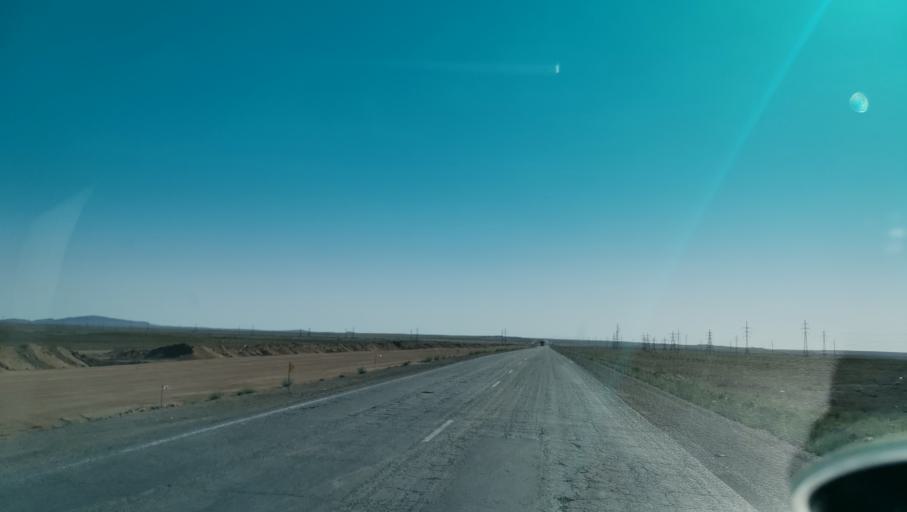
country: KZ
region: Qaraghandy
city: Balqash
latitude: 46.7279
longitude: 74.4960
